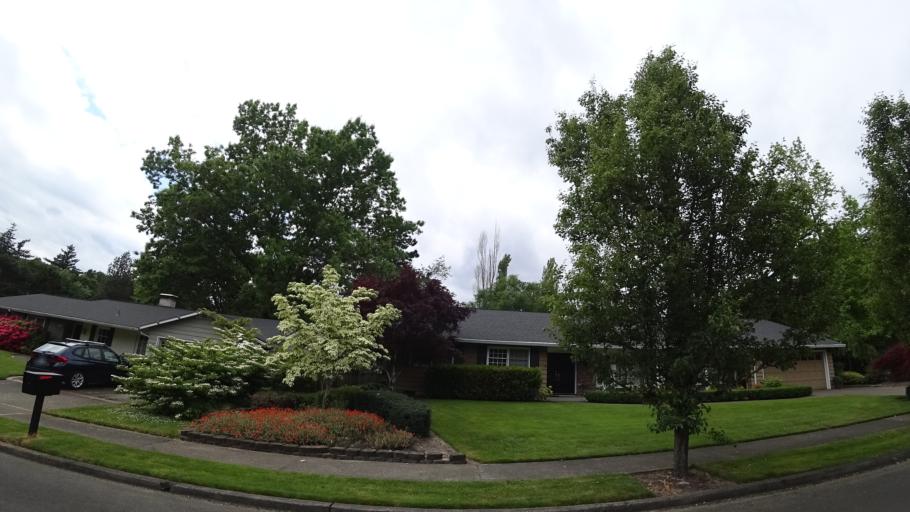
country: US
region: Oregon
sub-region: Washington County
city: Cedar Hills
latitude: 45.5016
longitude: -122.7920
